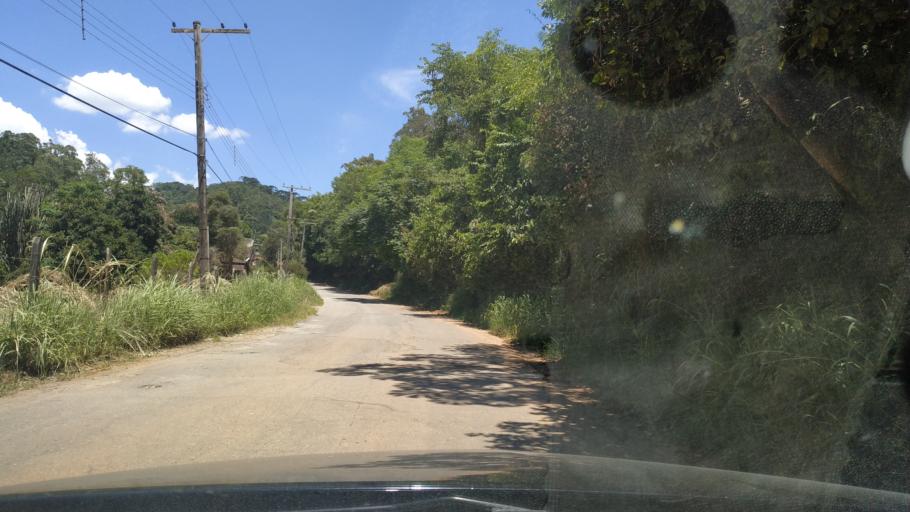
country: BR
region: Sao Paulo
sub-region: Campos Do Jordao
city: Campos do Jordao
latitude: -22.8032
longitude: -45.6928
